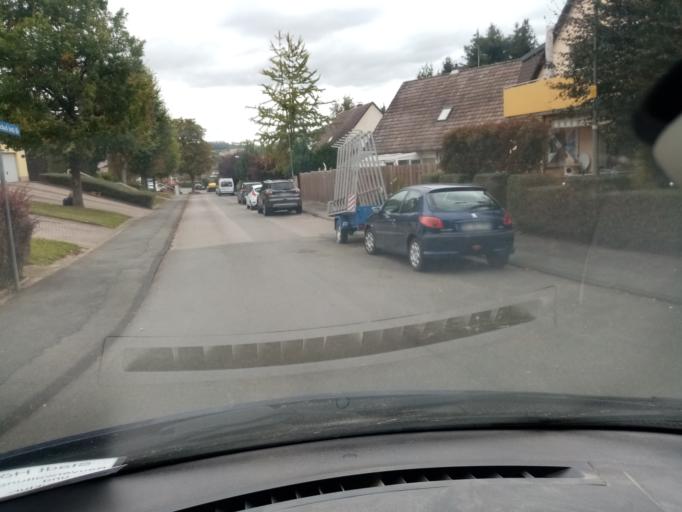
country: DE
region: North Rhine-Westphalia
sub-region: Regierungsbezirk Detmold
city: Hoexter
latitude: 51.7677
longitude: 9.3584
